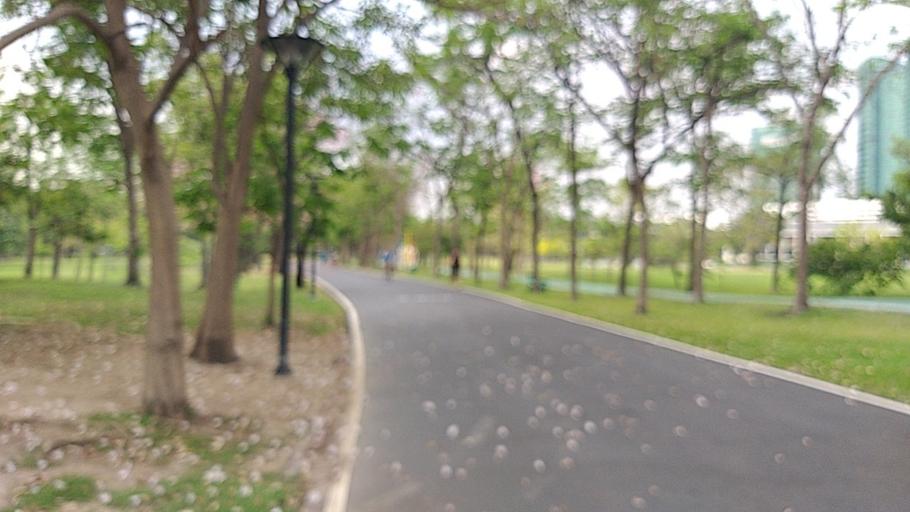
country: TH
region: Bangkok
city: Chatuchak
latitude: 13.8143
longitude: 100.5550
